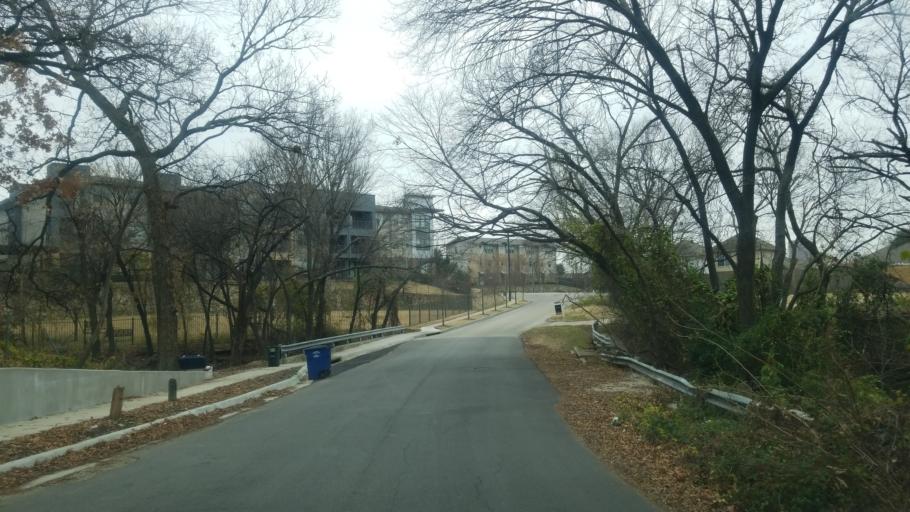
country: US
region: Texas
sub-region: Dallas County
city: Highland Park
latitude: 32.8168
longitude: -96.8261
